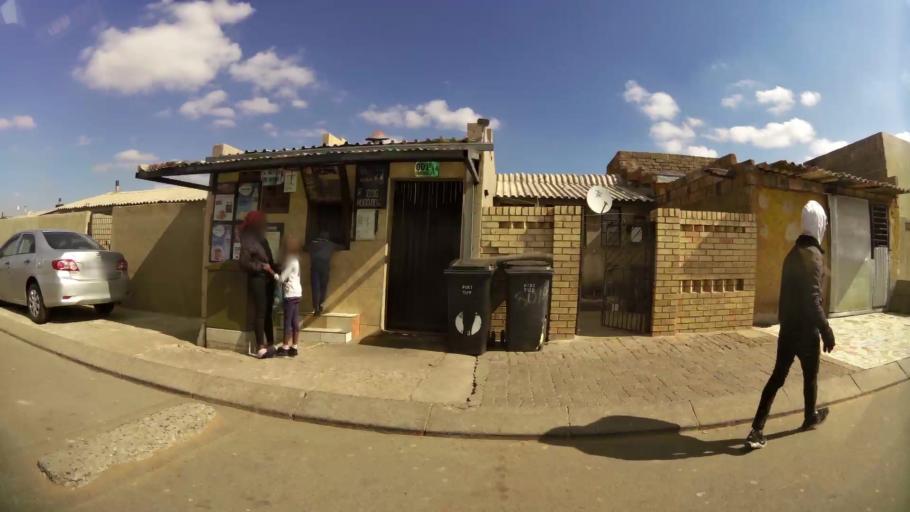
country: ZA
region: Gauteng
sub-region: City of Johannesburg Metropolitan Municipality
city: Soweto
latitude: -26.2331
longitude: 27.9010
